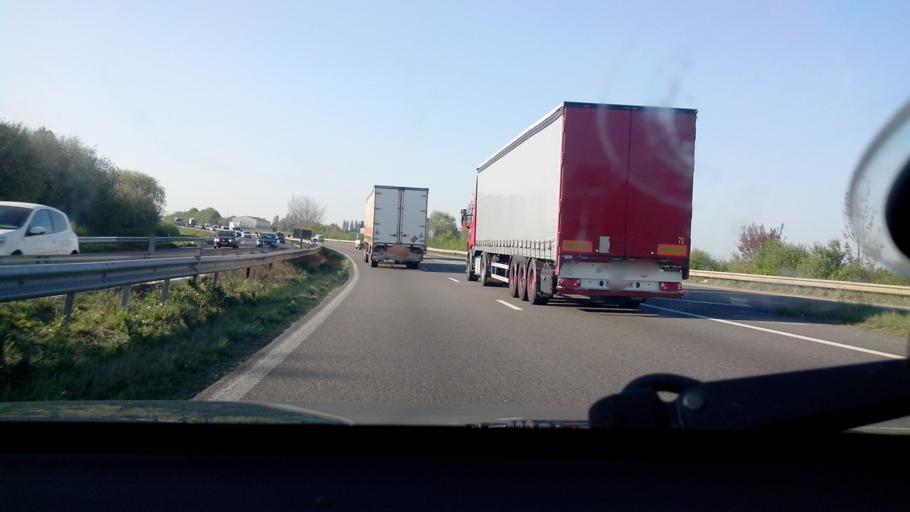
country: FR
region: Ile-de-France
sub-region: Departement de Seine-et-Marne
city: Servon
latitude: 48.7006
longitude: 2.5942
